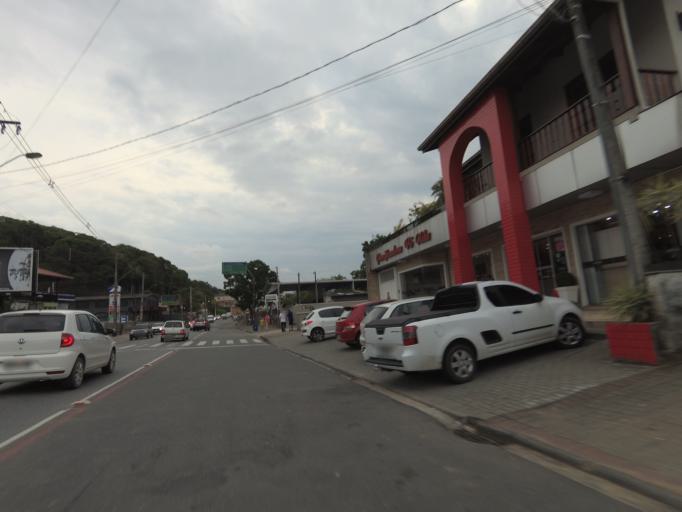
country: BR
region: Santa Catarina
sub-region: Blumenau
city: Blumenau
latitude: -26.8619
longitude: -49.0524
